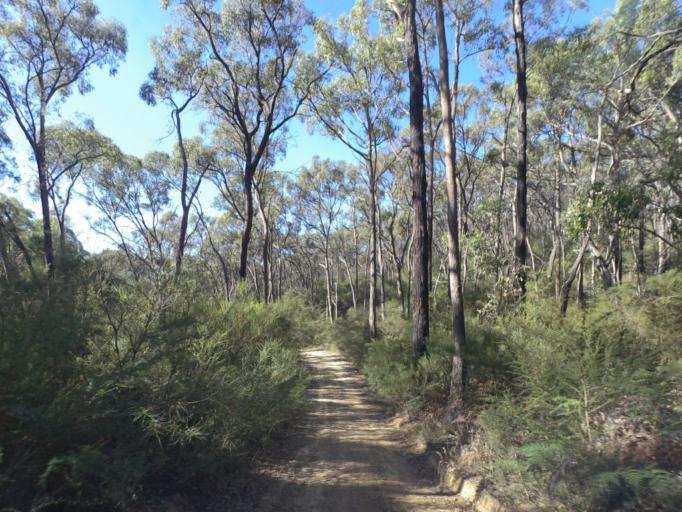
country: AU
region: Victoria
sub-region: Murrindindi
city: Kinglake West
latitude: -37.4707
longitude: 145.3644
